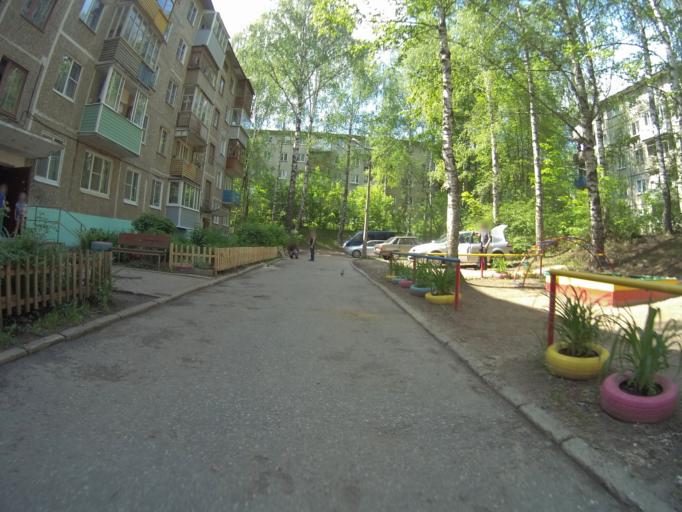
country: RU
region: Vladimir
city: Vladimir
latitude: 56.1281
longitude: 40.3536
